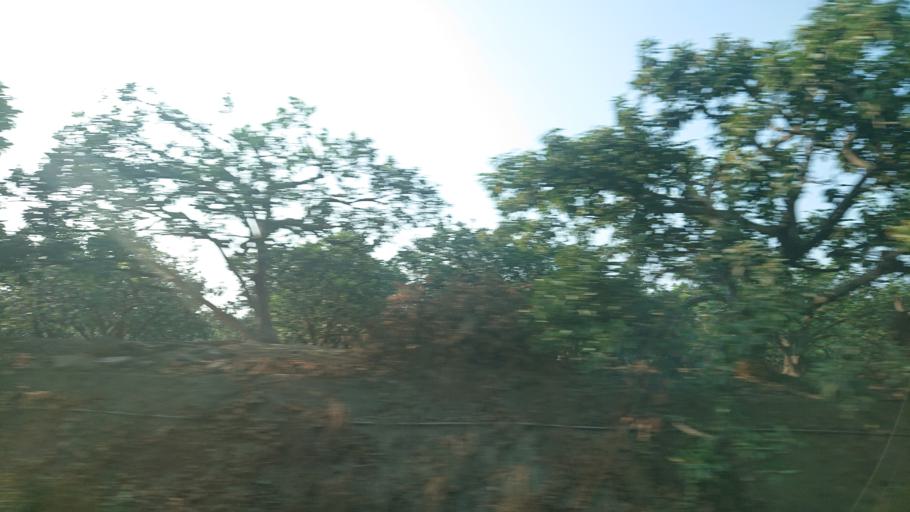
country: TW
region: Taiwan
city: Xinying
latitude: 23.1663
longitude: 120.2527
